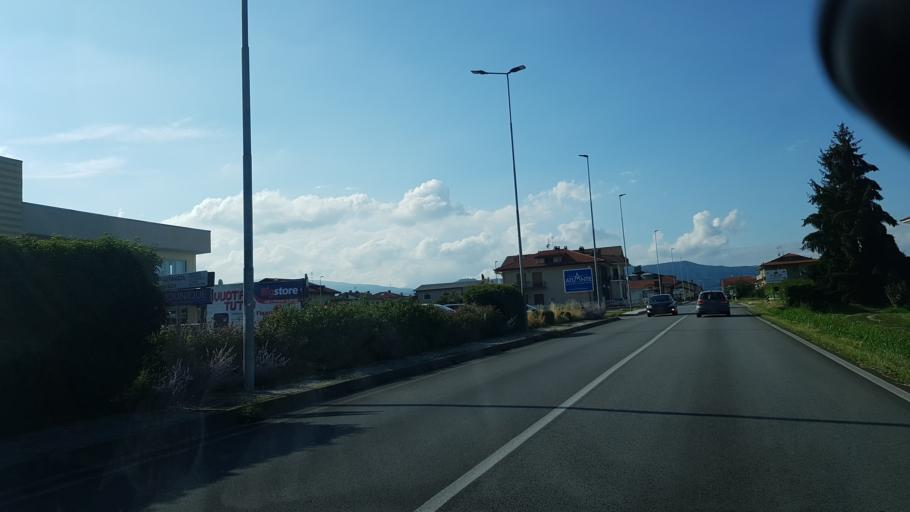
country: IT
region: Piedmont
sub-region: Provincia di Cuneo
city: Roata Rossi
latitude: 44.4745
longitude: 7.5091
